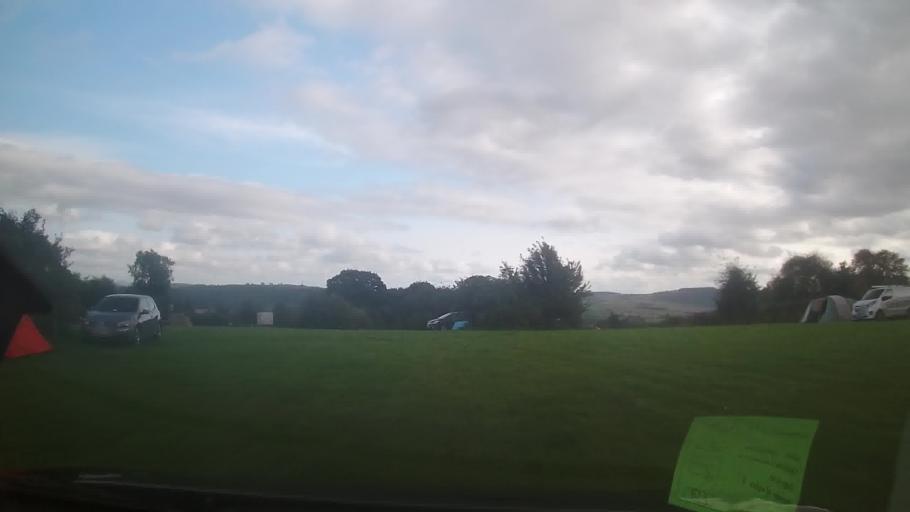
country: GB
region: England
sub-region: Shropshire
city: Bishop's Castle
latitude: 52.5014
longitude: -2.9992
